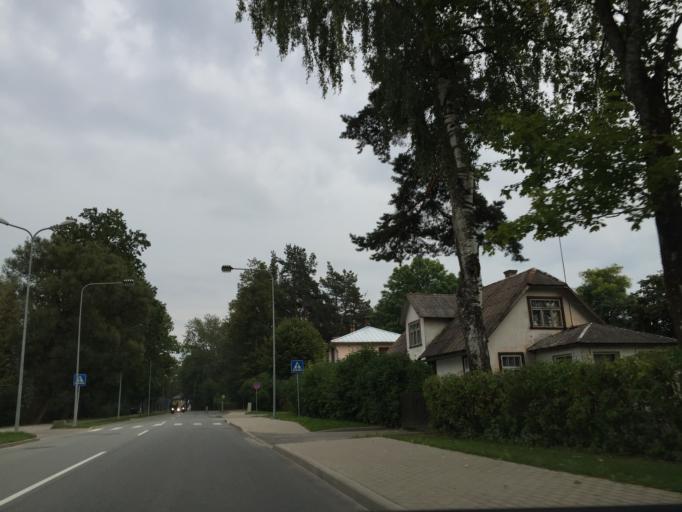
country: LV
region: Ogre
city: Ogre
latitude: 56.8131
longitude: 24.6335
